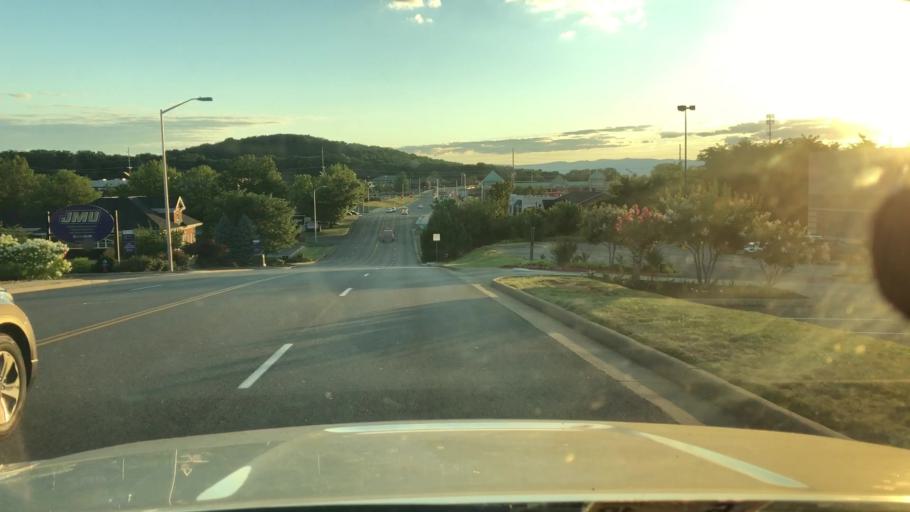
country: US
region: Virginia
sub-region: City of Harrisonburg
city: Harrisonburg
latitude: 38.4294
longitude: -78.8521
